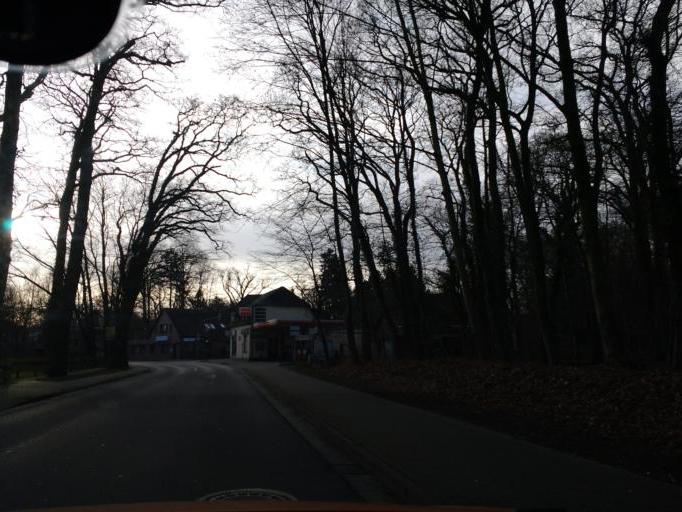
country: DE
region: Lower Saxony
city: Hude
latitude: 53.1166
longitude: 8.4535
